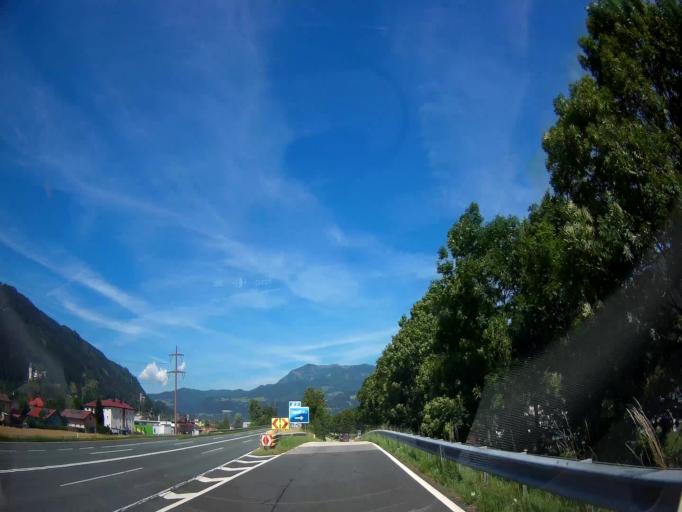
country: AT
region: Carinthia
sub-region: Politischer Bezirk Sankt Veit an der Glan
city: Friesach
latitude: 46.9505
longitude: 14.4236
